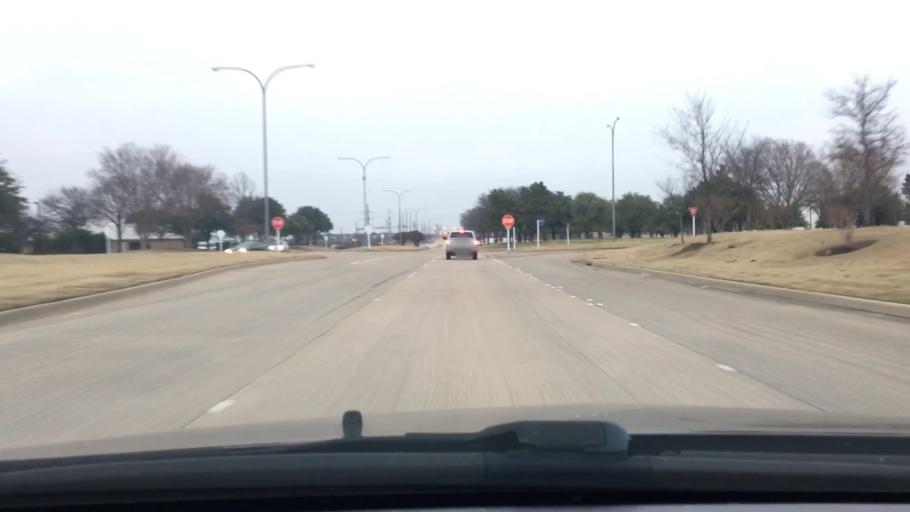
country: US
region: Texas
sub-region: Tarrant County
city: Keller
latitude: 32.9760
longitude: -97.2627
